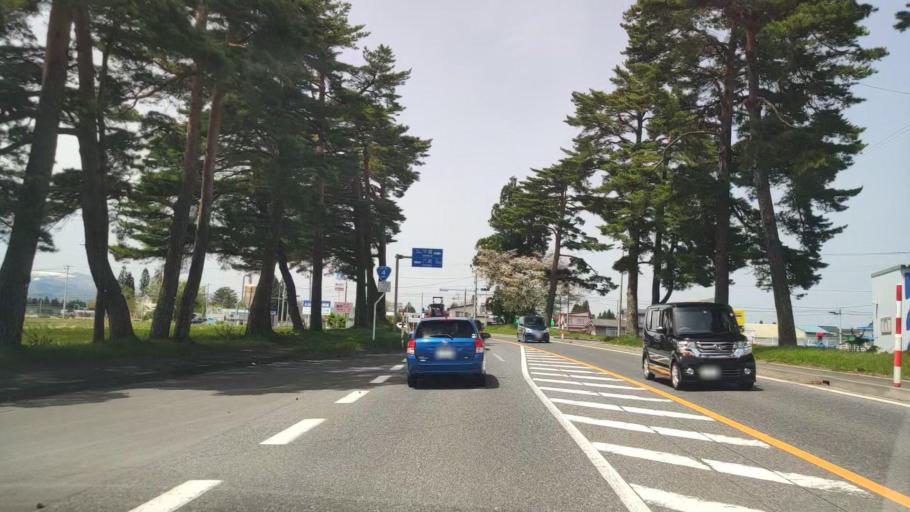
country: JP
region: Aomori
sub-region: Misawa Shi
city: Inuotose
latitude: 40.6722
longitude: 141.1822
